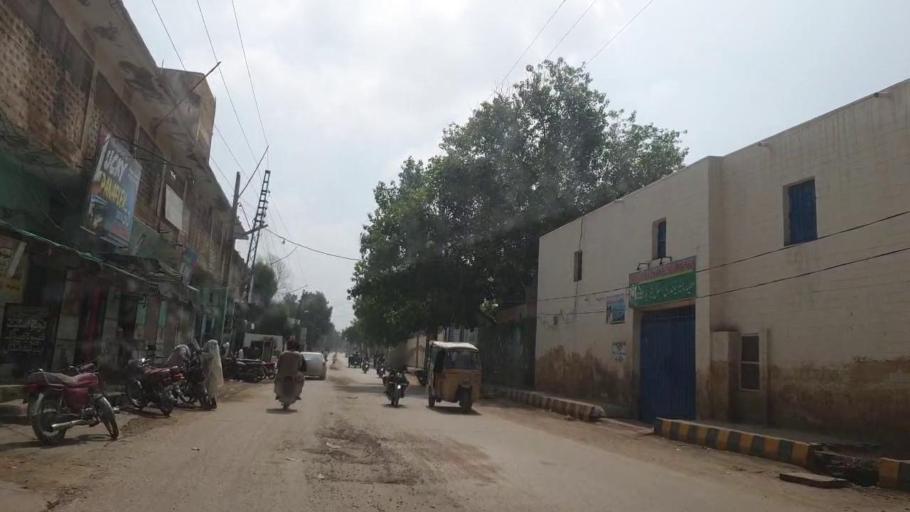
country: PK
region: Sindh
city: Khairpur
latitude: 27.5240
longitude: 68.7437
